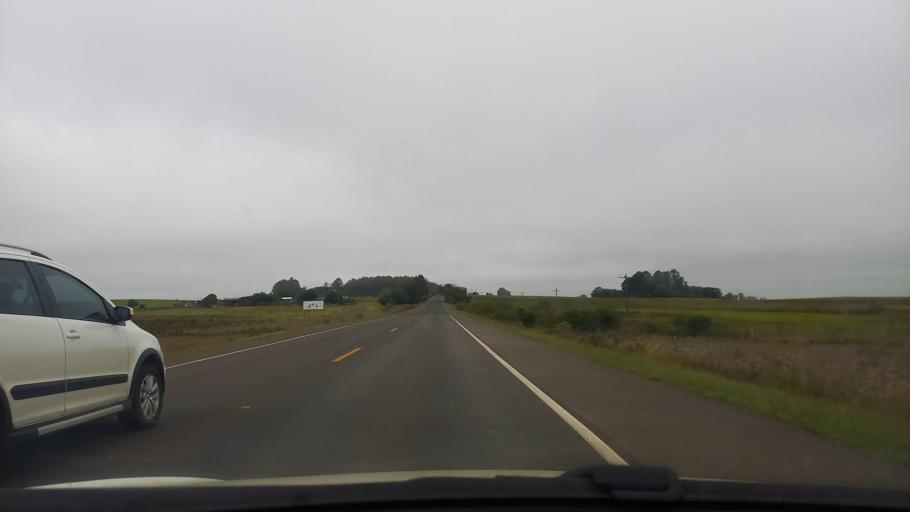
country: BR
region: Rio Grande do Sul
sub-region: Rosario Do Sul
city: Rosario do Sul
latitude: -30.3188
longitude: -55.0001
